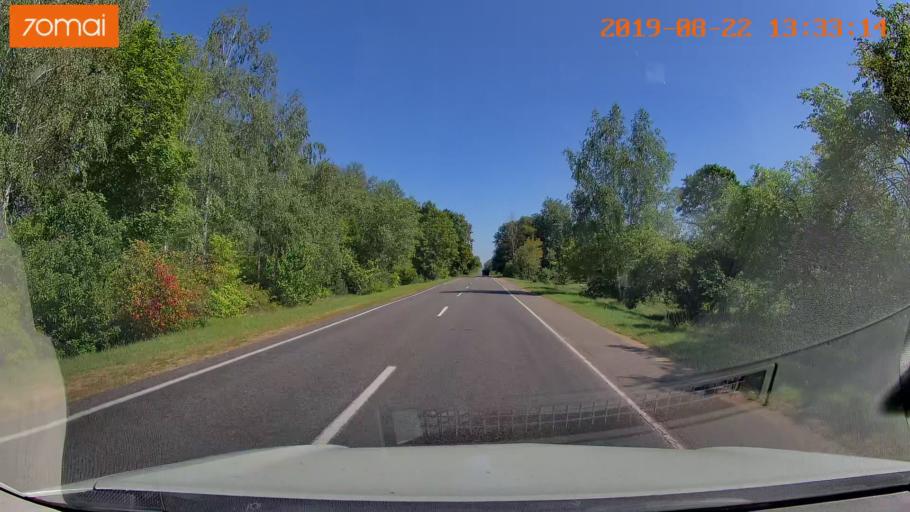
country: BY
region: Minsk
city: Staryya Darohi
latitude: 53.2167
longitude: 28.2203
